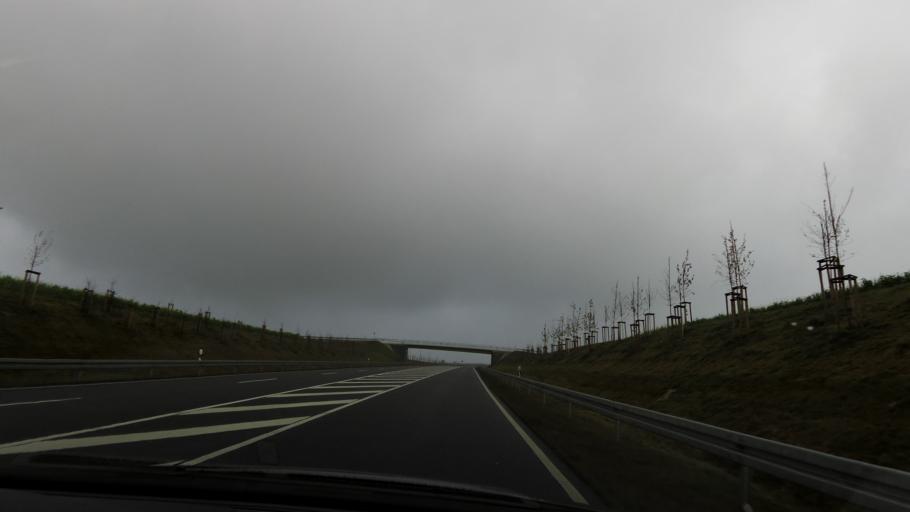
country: DE
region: North Rhine-Westphalia
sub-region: Regierungsbezirk Koln
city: Gangelt
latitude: 51.0171
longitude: 6.0495
